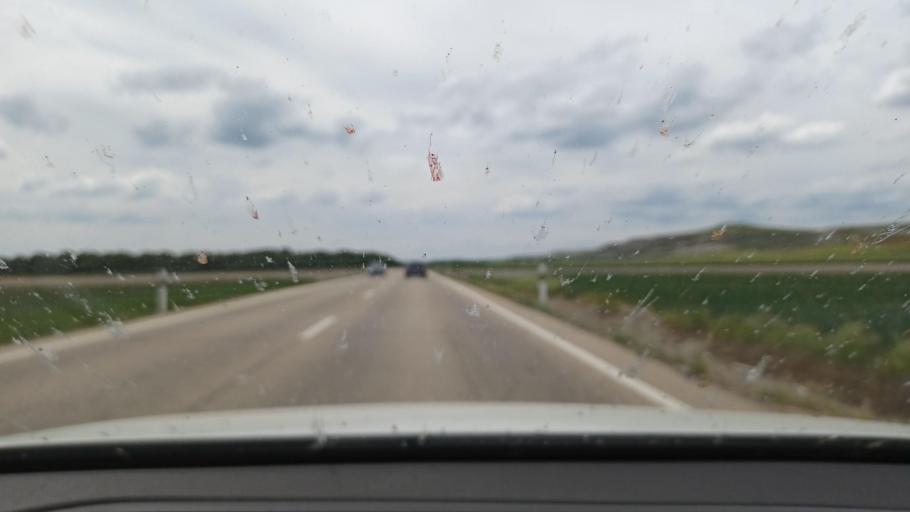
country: ES
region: Castille and Leon
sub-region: Provincia de Segovia
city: Frumales
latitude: 41.3822
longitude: -4.2123
